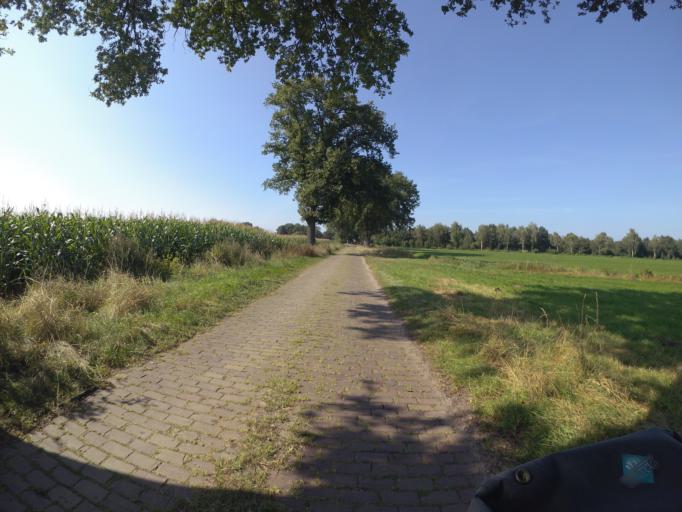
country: NL
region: North Brabant
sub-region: Gemeente Uden
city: Odiliapeel
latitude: 51.6683
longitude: 5.7119
